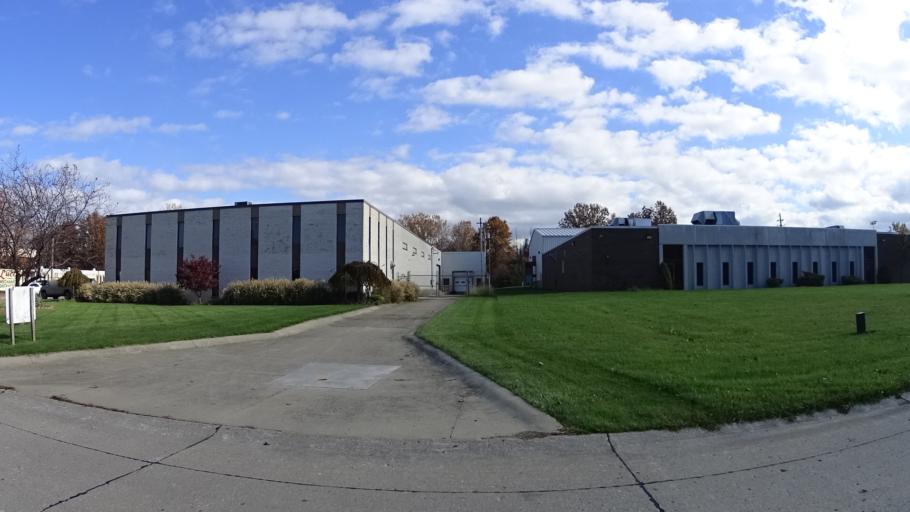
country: US
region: Ohio
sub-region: Lorain County
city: Lorain
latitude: 41.4478
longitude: -82.2125
